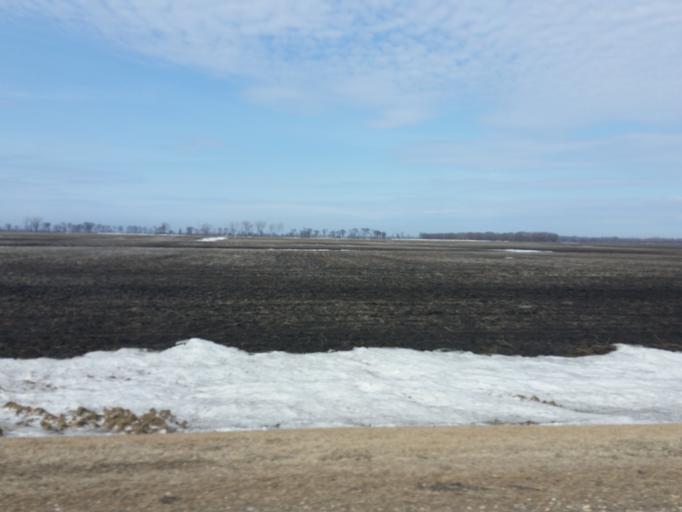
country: US
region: North Dakota
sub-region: Walsh County
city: Grafton
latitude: 48.4266
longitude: -97.2280
